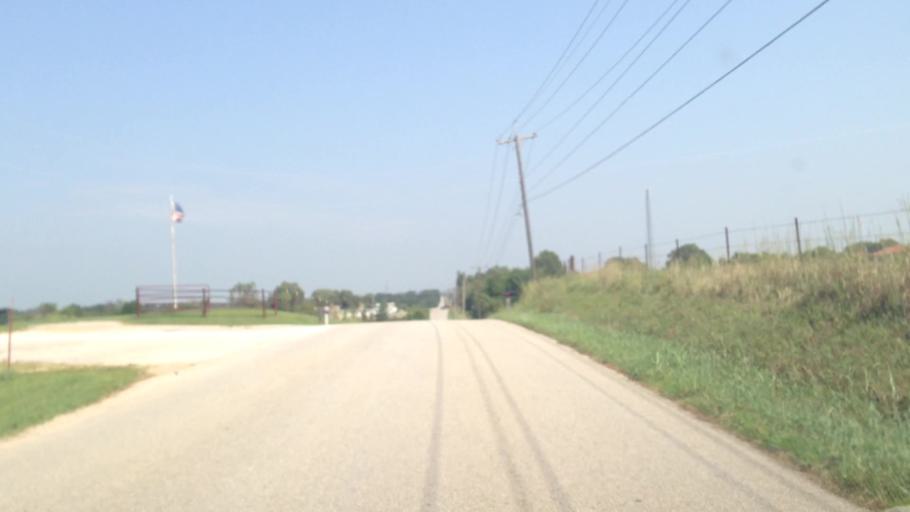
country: US
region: Oklahoma
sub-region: Craig County
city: Vinita
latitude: 36.6519
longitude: -95.1256
